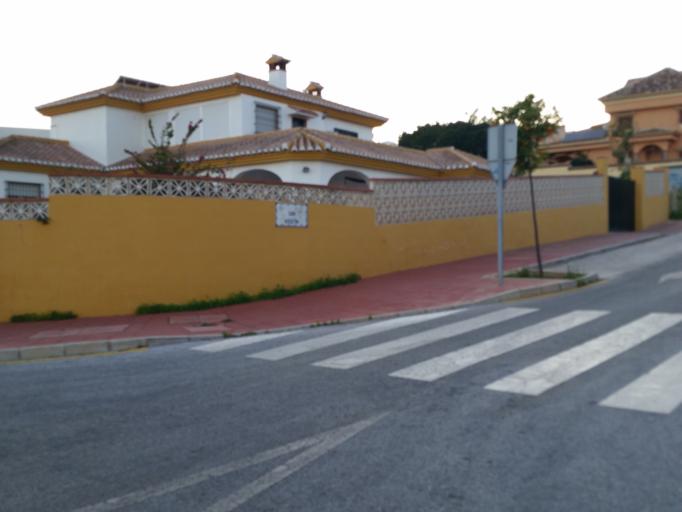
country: ES
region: Andalusia
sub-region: Provincia de Malaga
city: Torremolinos
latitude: 36.6052
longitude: -4.5275
